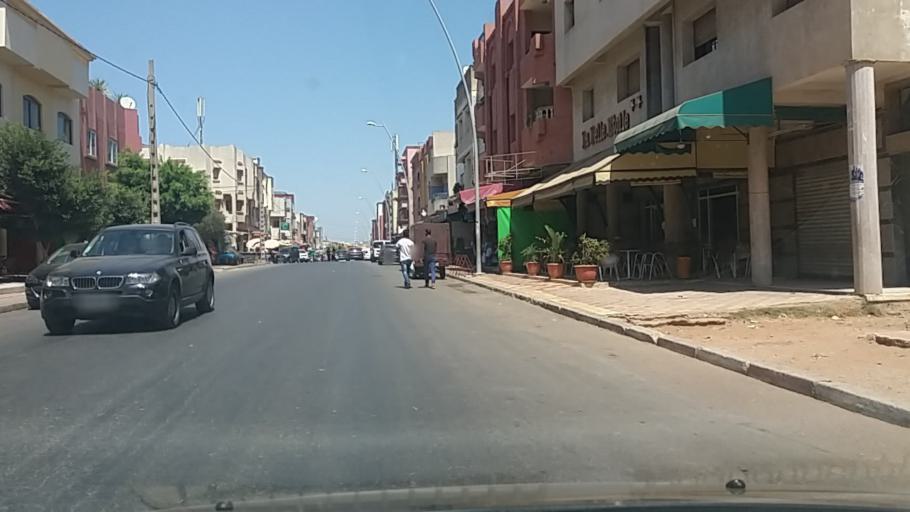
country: MA
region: Gharb-Chrarda-Beni Hssen
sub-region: Kenitra Province
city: Kenitra
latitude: 34.2592
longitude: -6.6208
